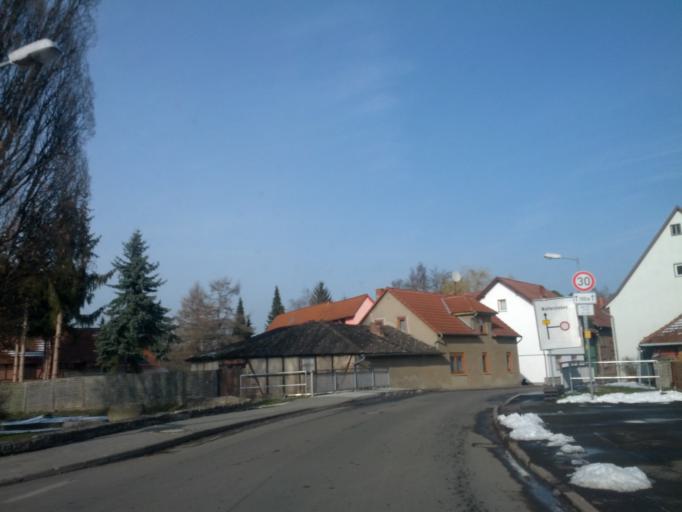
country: DE
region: Thuringia
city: Kirchheim
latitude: 50.9204
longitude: 10.9903
